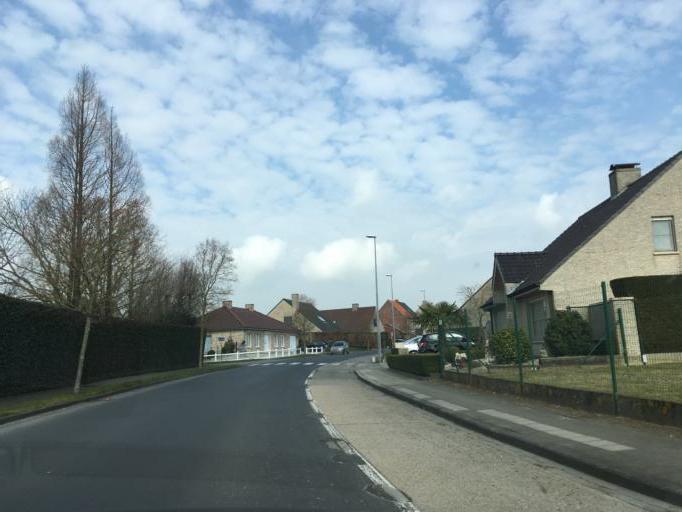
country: BE
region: Flanders
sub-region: Provincie West-Vlaanderen
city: Izegem
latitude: 50.9355
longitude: 3.1888
